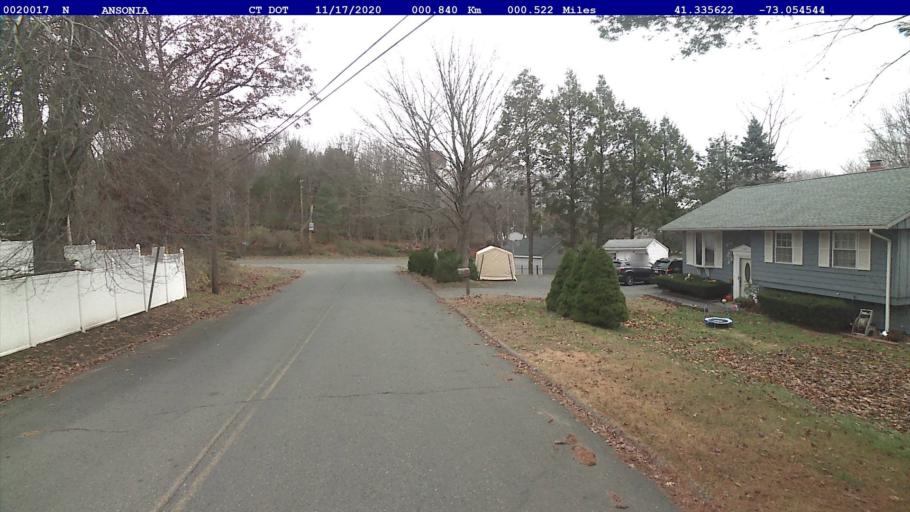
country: US
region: Connecticut
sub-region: New Haven County
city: Ansonia
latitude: 41.3356
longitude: -73.0546
